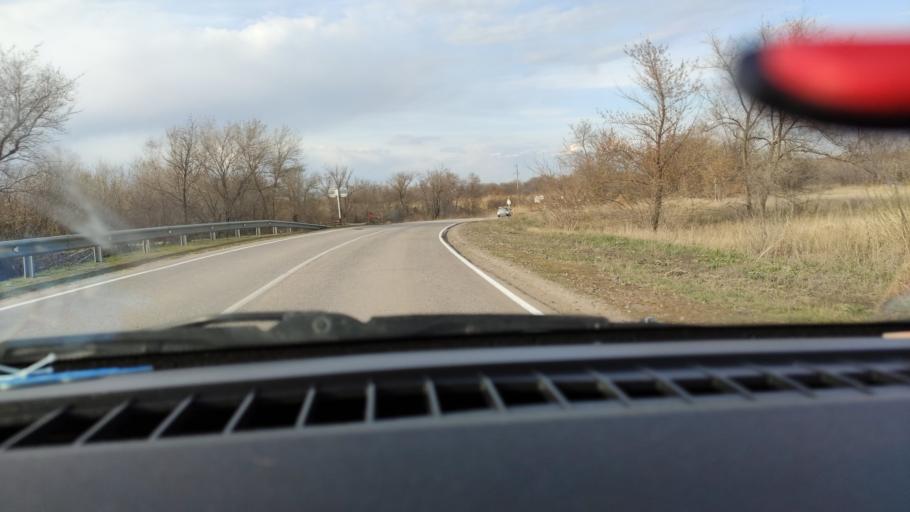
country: RU
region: Saratov
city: Privolzhskiy
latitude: 51.2388
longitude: 45.9269
